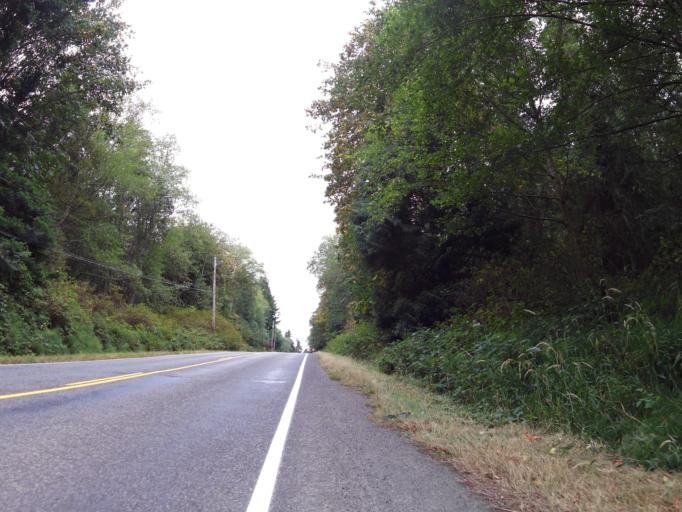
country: US
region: Washington
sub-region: Kitsap County
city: Lofall
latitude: 47.8743
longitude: -122.6362
